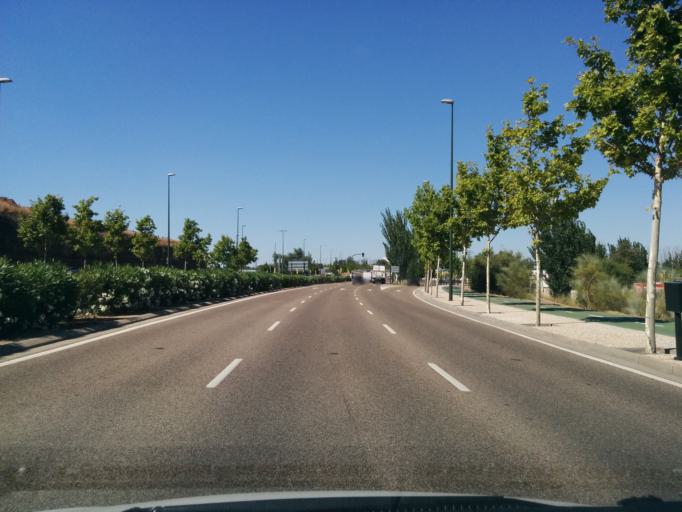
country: ES
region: Aragon
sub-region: Provincia de Zaragoza
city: Zaragoza
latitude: 41.6431
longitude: -0.8577
